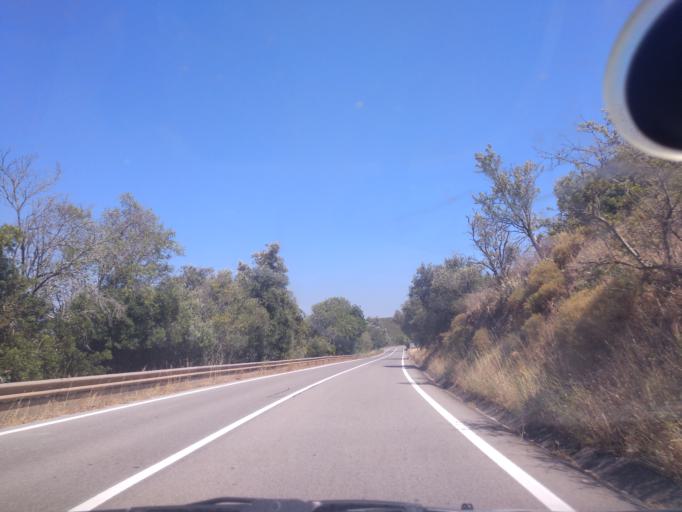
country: PT
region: Faro
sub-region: Lagos
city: Lagos
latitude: 37.1558
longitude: -8.7243
